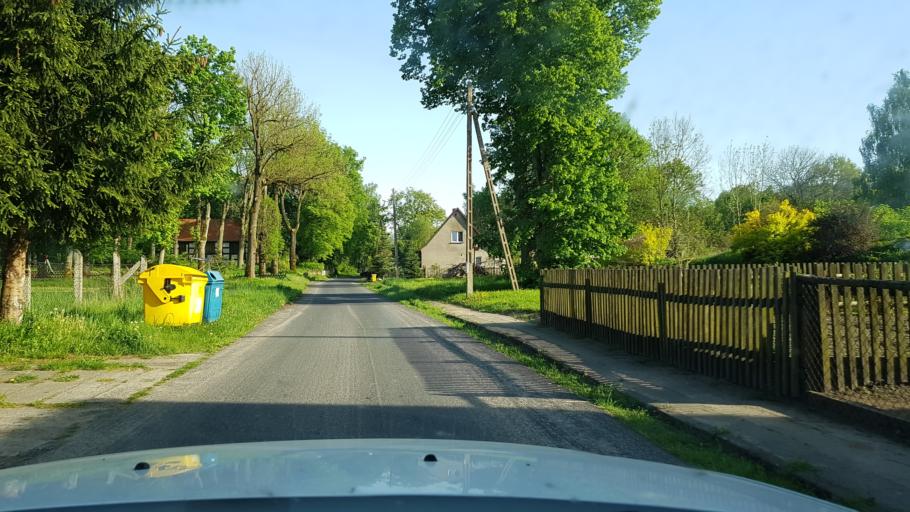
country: PL
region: West Pomeranian Voivodeship
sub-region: Powiat lobeski
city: Radowo Male
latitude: 53.6800
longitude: 15.3496
